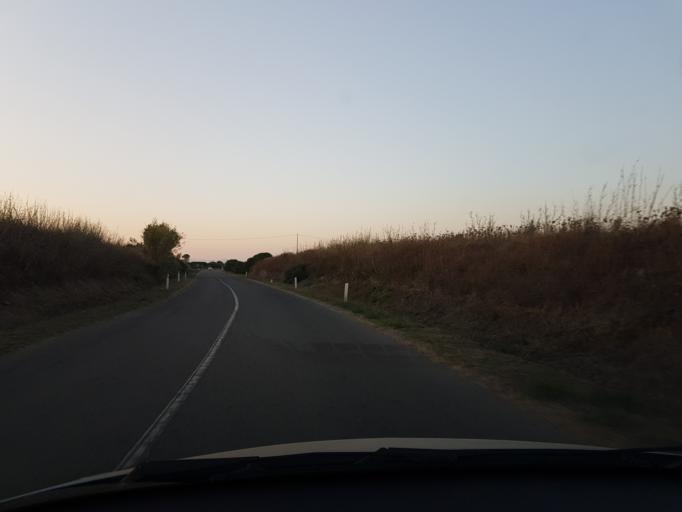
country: IT
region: Sardinia
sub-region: Provincia di Oristano
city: Nurachi
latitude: 39.9780
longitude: 8.4543
